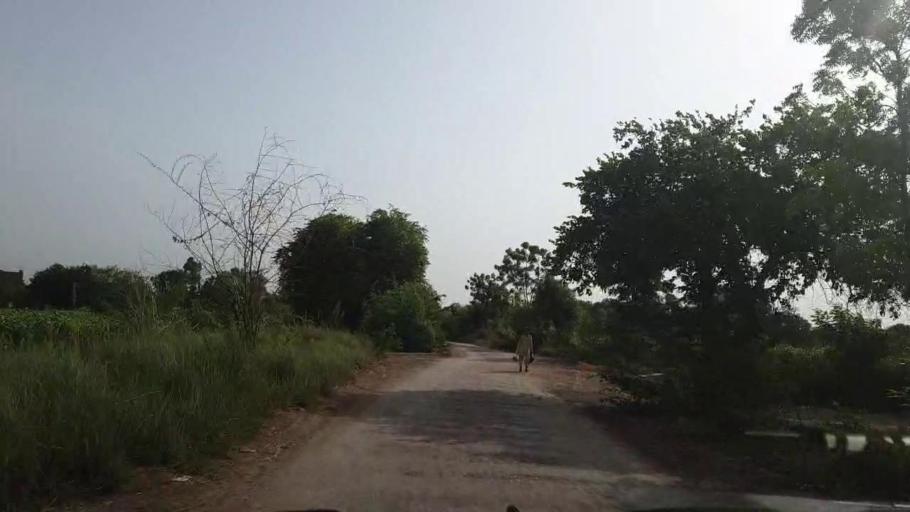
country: PK
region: Sindh
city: Nawabshah
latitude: 26.2300
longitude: 68.4066
